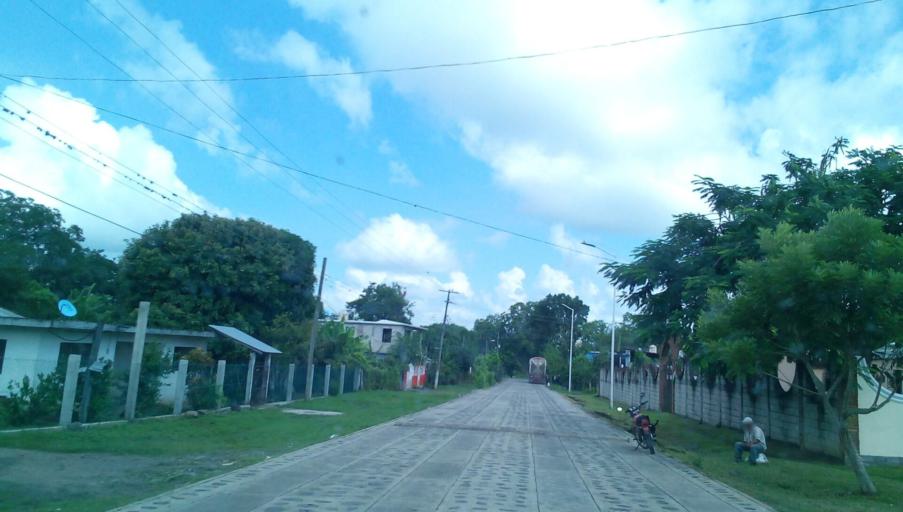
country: MX
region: Veracruz
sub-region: Citlaltepetl
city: Las Sabinas
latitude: 21.3623
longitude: -97.9013
